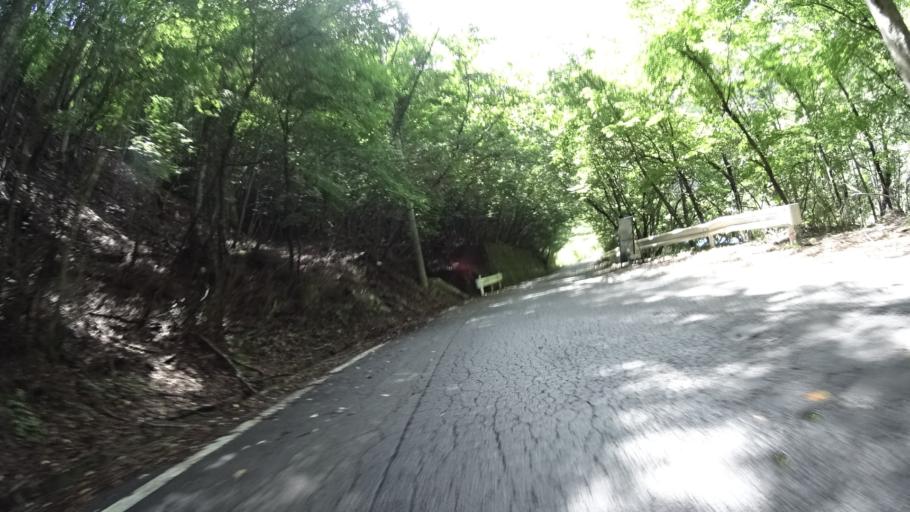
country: JP
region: Yamanashi
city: Enzan
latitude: 35.6754
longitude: 138.8074
